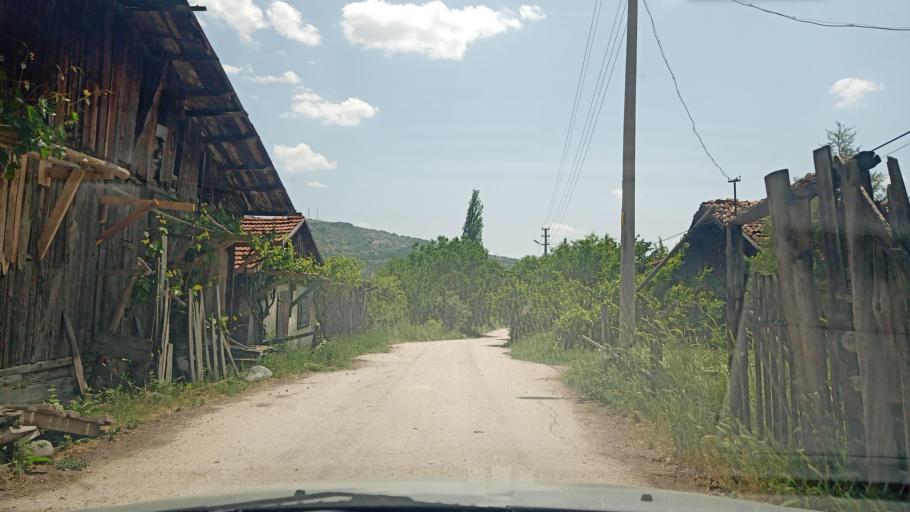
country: TR
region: Bolu
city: Seben
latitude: 40.4122
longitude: 31.5789
